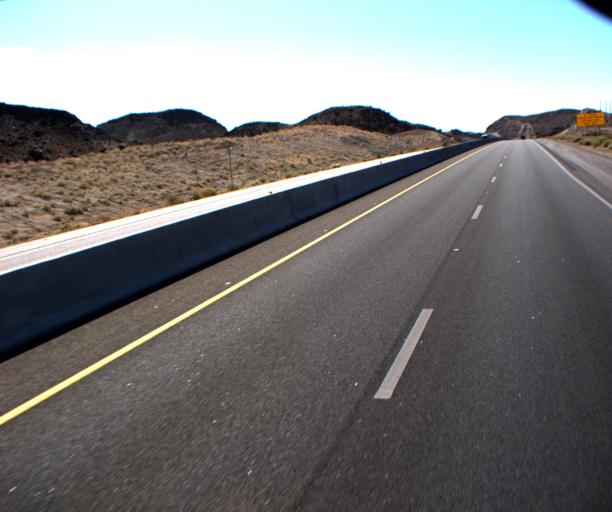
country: US
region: Nevada
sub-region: Clark County
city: Boulder City
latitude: 35.9945
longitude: -114.7186
